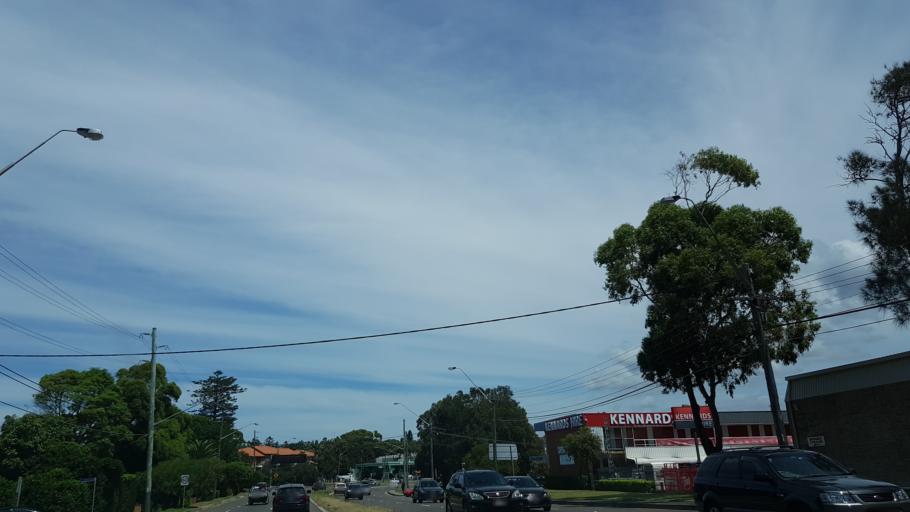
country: AU
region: New South Wales
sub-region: Pittwater
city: Bay View
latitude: -33.6746
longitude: 151.3104
